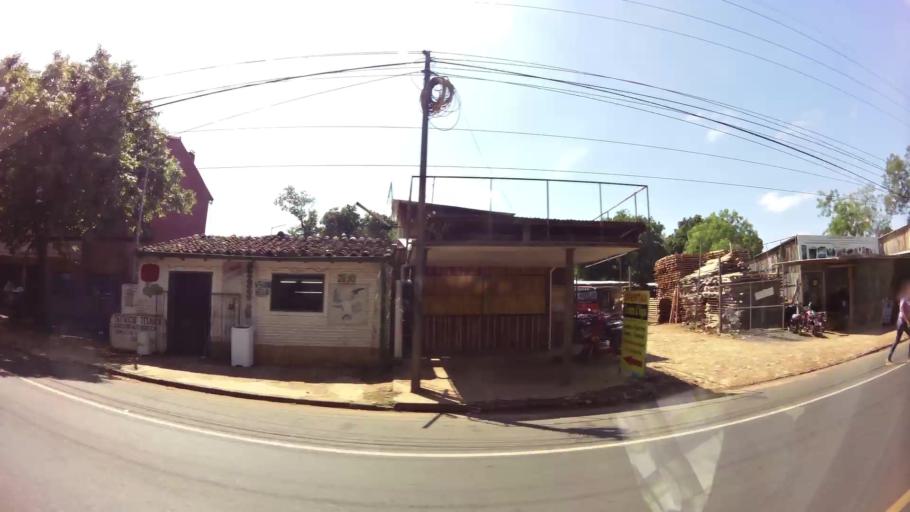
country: PY
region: Central
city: San Lorenzo
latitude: -25.3044
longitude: -57.5046
